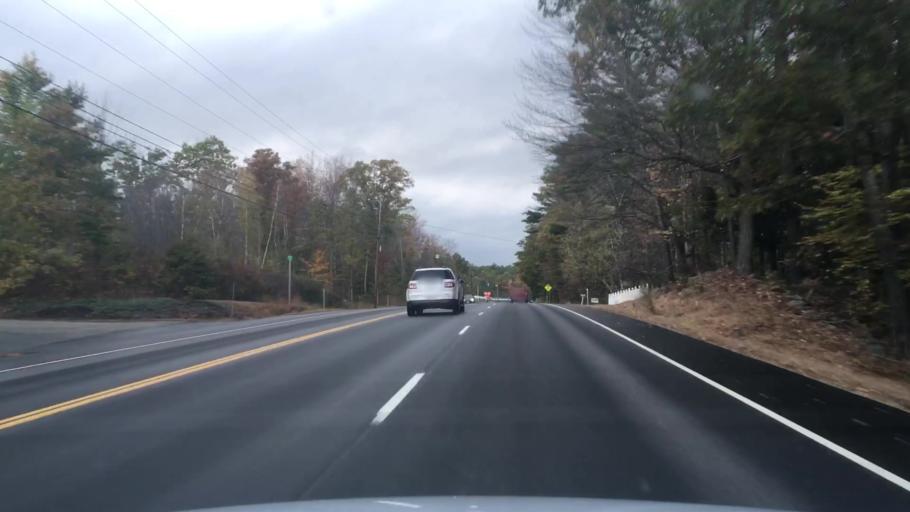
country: US
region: New Hampshire
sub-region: Merrimack County
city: Chichester
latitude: 43.2330
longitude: -71.3790
